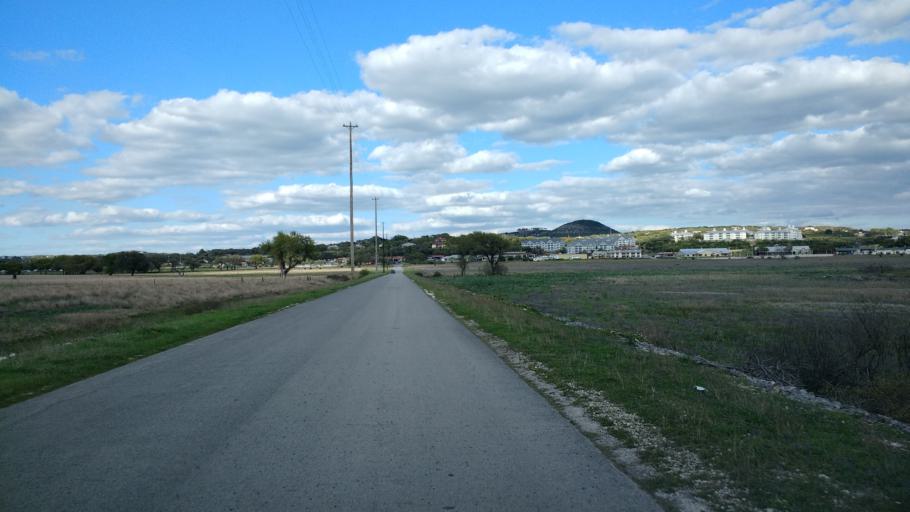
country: US
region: Texas
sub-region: Comal County
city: Canyon Lake
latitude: 29.9094
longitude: -98.2221
